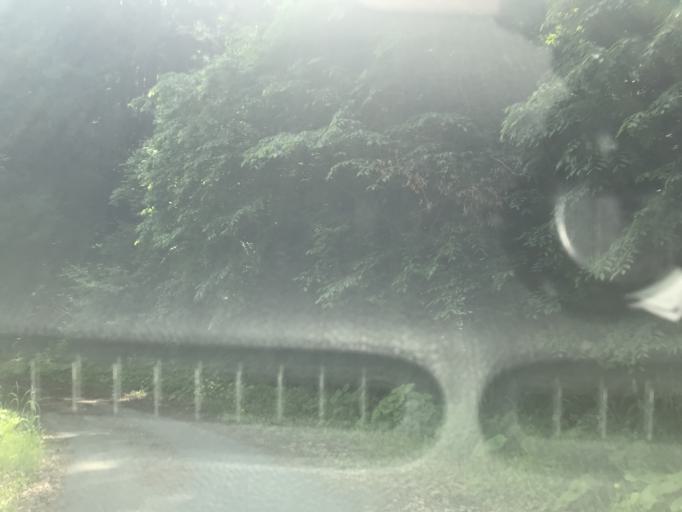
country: JP
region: Iwate
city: Ichinoseki
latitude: 38.9520
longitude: 141.2427
